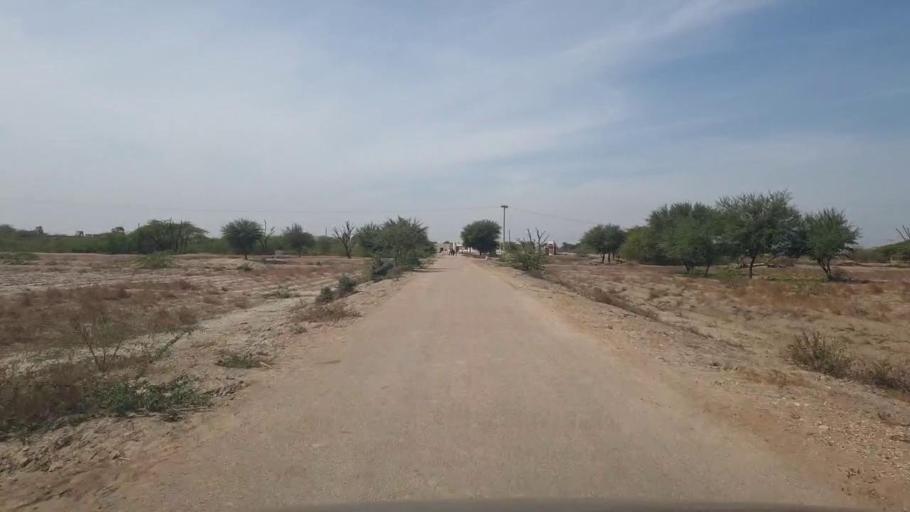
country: PK
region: Sindh
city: Kunri
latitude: 25.3342
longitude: 69.5815
